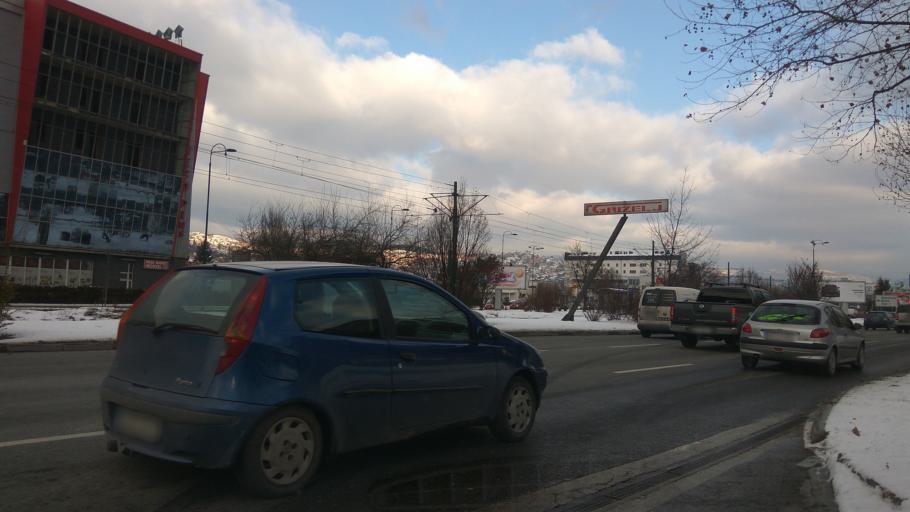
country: BA
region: Federation of Bosnia and Herzegovina
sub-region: Kanton Sarajevo
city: Sarajevo
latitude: 43.8435
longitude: 18.3327
